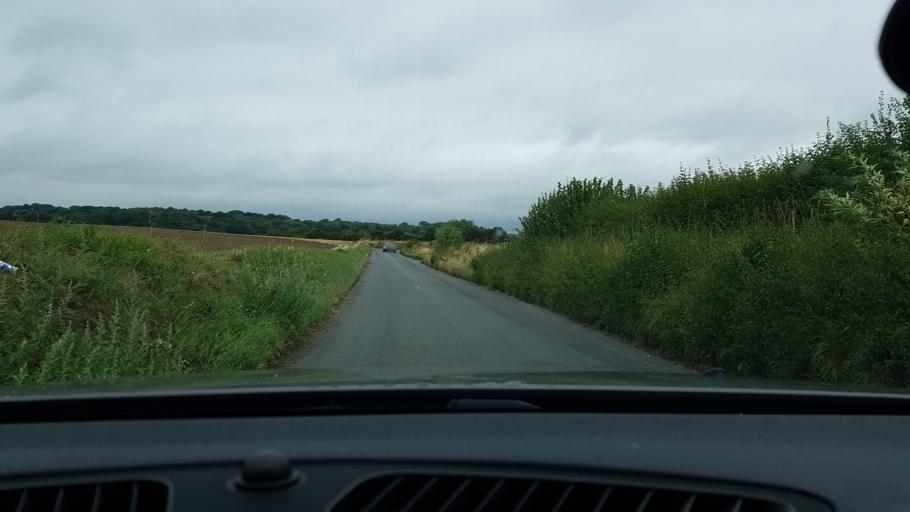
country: GB
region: England
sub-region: Wiltshire
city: Shalbourne
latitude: 51.3748
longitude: -1.5345
